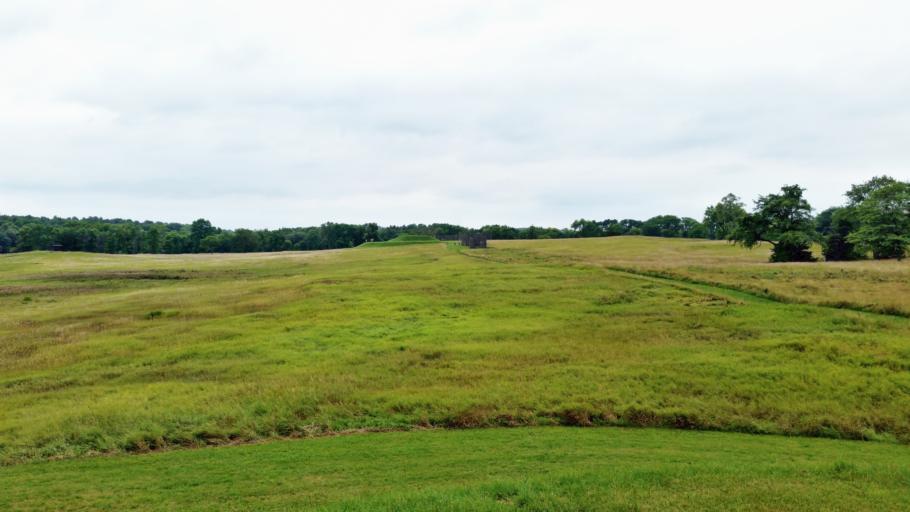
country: US
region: Wisconsin
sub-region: Jefferson County
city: Lake Mills
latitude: 43.0677
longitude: -88.8609
